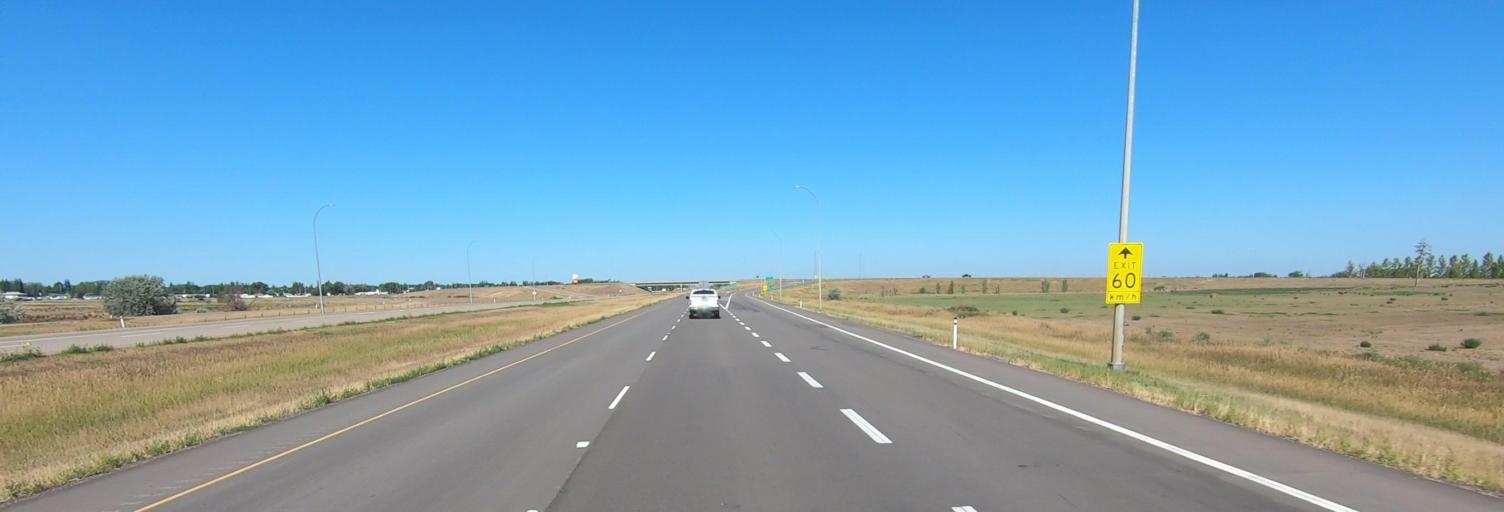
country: CA
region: Alberta
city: Brooks
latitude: 50.5683
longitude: -111.8550
